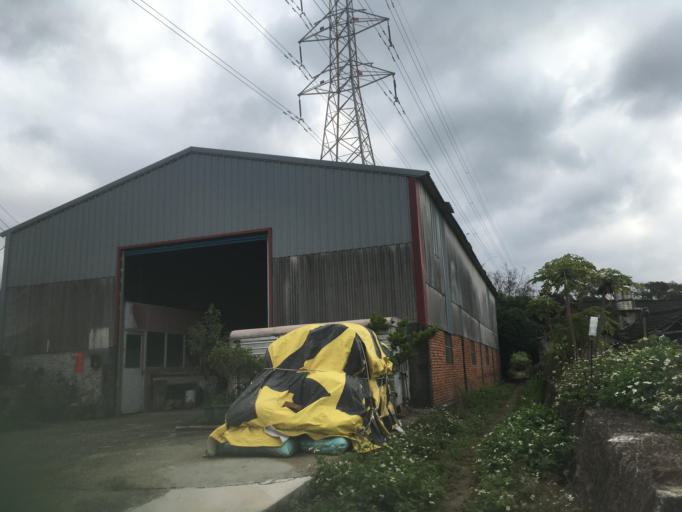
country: TW
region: Taiwan
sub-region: Miaoli
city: Miaoli
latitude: 24.4452
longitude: 120.7131
